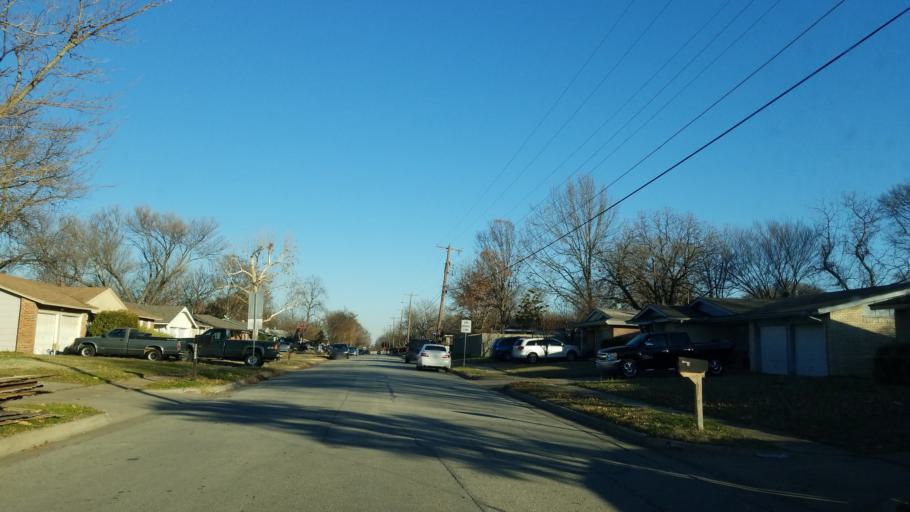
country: US
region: Texas
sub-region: Tarrant County
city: Arlington
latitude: 32.7281
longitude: -97.0679
